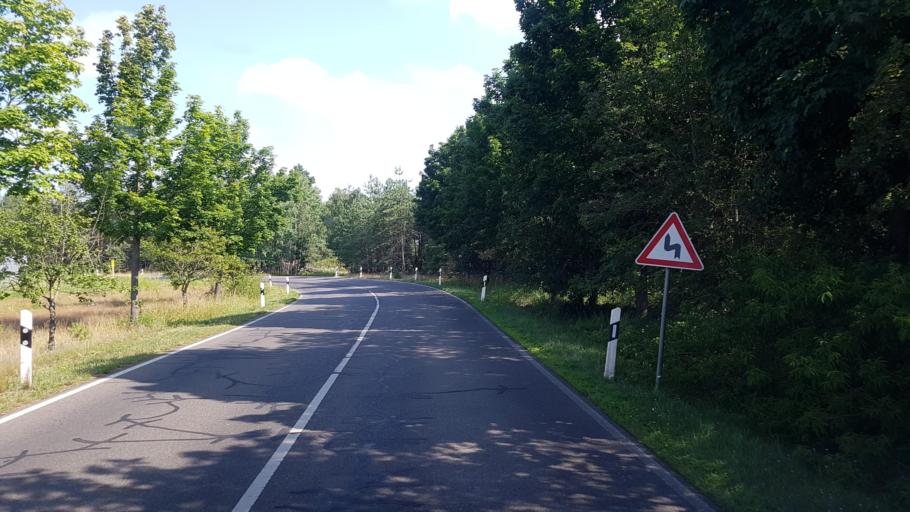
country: DE
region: Brandenburg
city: Grossraschen
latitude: 51.5929
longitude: 14.0284
